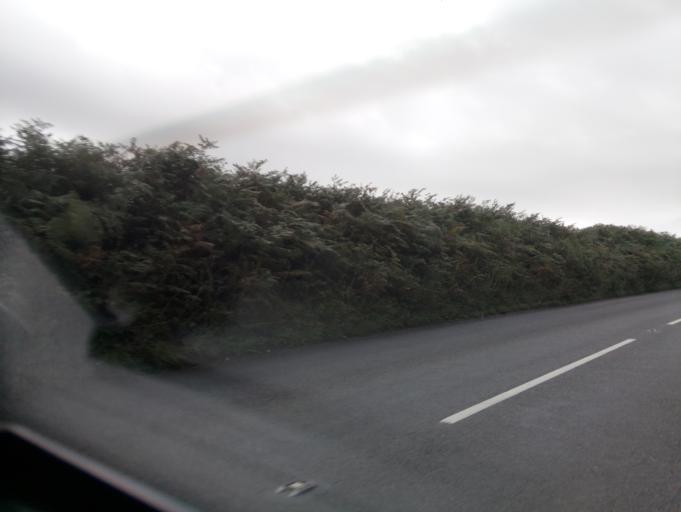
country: GB
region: England
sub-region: Devon
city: Kingsbridge
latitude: 50.2926
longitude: -3.7860
